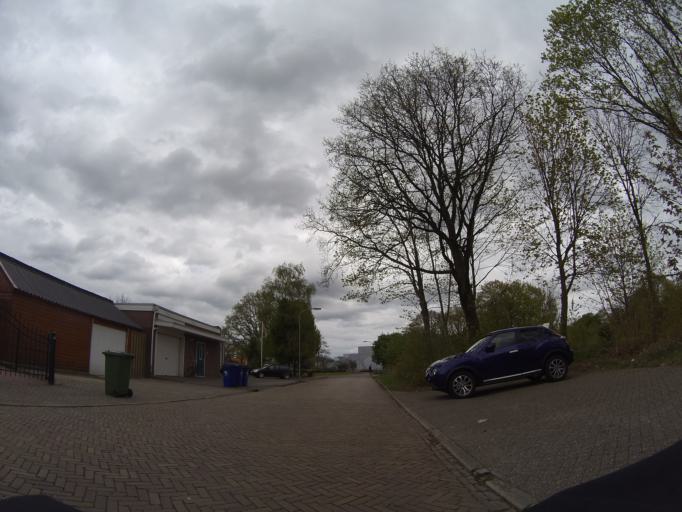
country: NL
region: Drenthe
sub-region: Gemeente Emmen
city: Emmen
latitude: 52.7937
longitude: 6.8996
